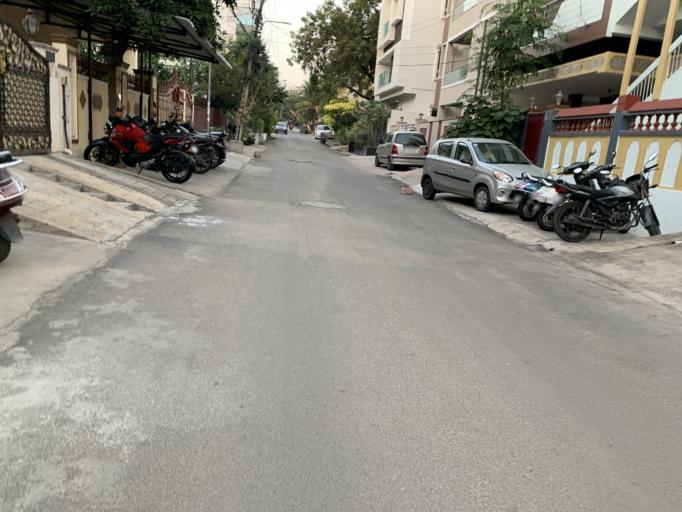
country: IN
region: Telangana
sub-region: Rangareddi
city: Kukatpalli
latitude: 17.4952
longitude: 78.3832
